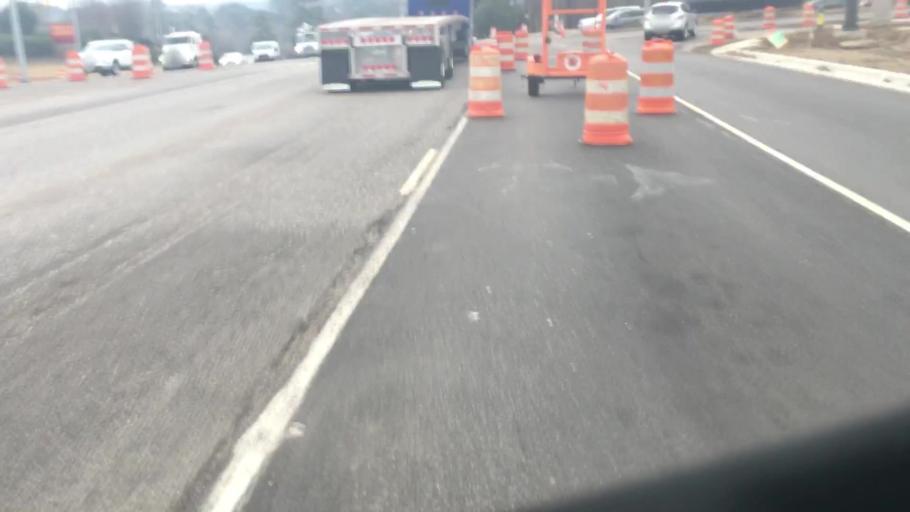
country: US
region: Alabama
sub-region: Shelby County
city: Helena
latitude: 33.3545
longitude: -86.8463
